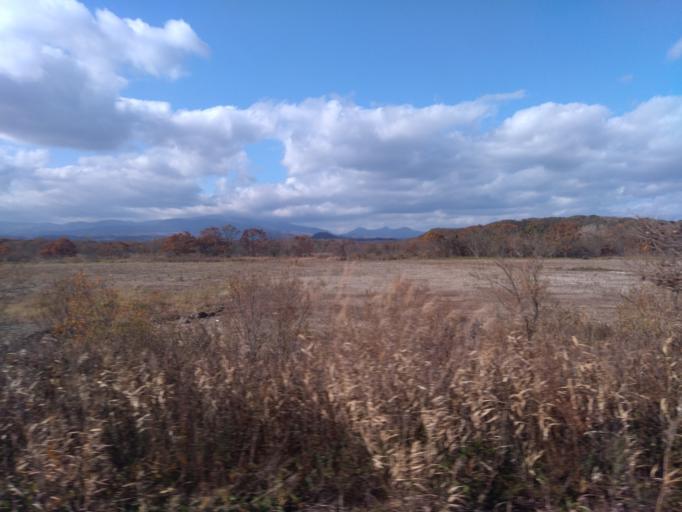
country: JP
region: Hokkaido
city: Shiraoi
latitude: 42.5336
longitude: 141.3257
